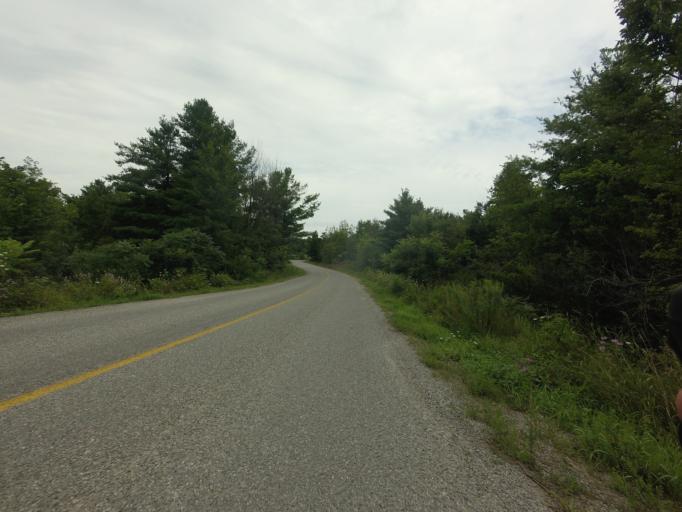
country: CA
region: Ontario
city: Kingston
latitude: 44.5950
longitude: -76.6390
